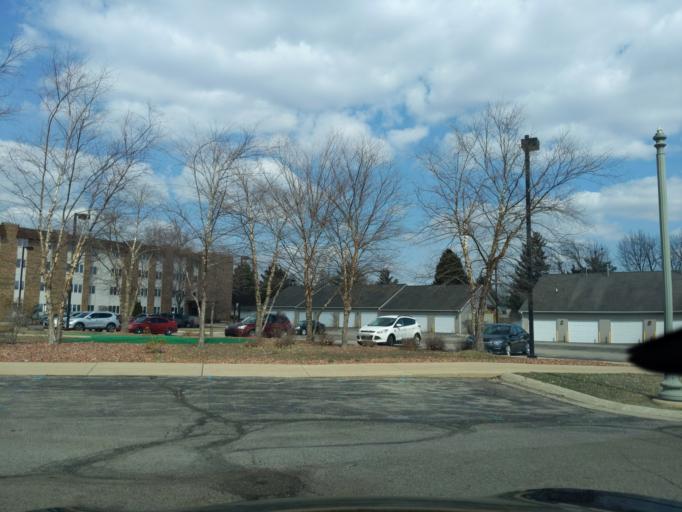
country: US
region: Michigan
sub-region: Jackson County
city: Jackson
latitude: 42.2745
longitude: -84.4416
